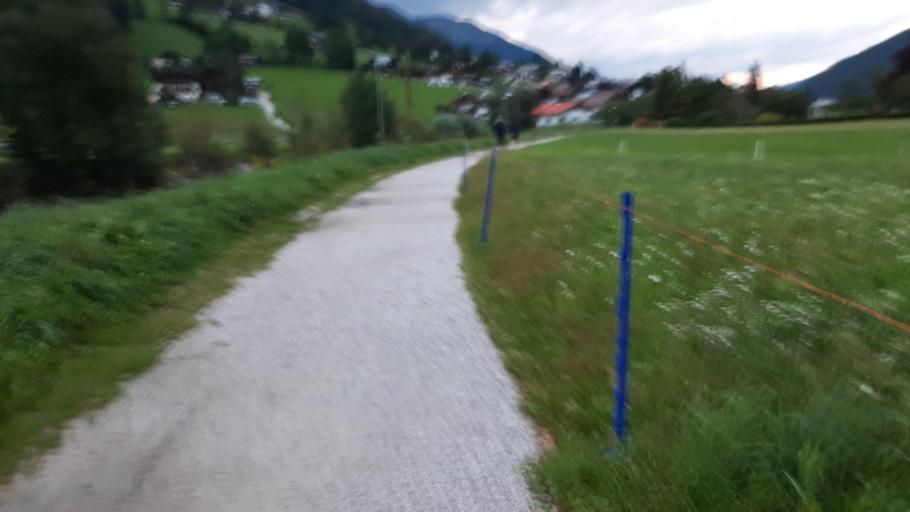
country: AT
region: Tyrol
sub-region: Politischer Bezirk Innsbruck Land
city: Neustift im Stubaital
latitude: 47.1204
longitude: 11.3234
